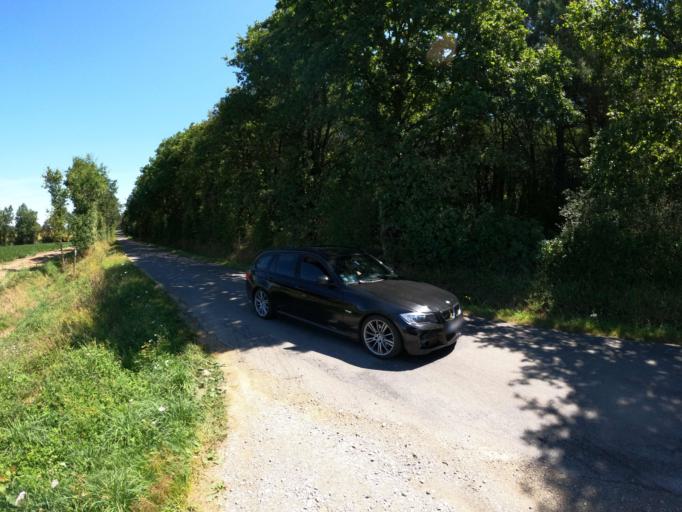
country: FR
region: Pays de la Loire
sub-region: Departement de la Loire-Atlantique
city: Lege
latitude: 46.9389
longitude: -1.6298
